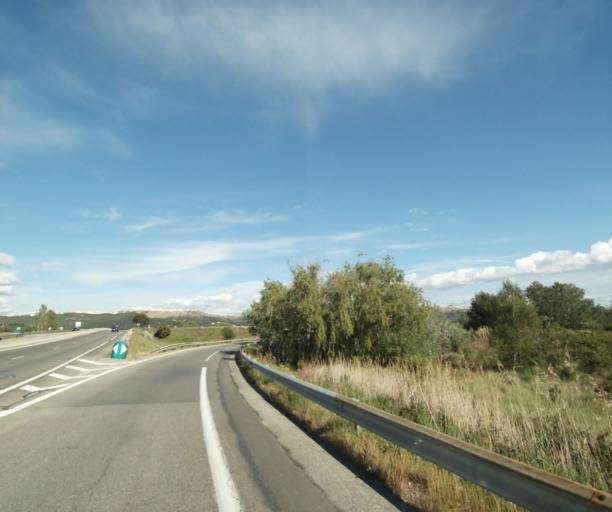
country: FR
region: Provence-Alpes-Cote d'Azur
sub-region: Departement des Bouches-du-Rhone
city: Rognac
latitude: 43.4932
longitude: 5.2147
